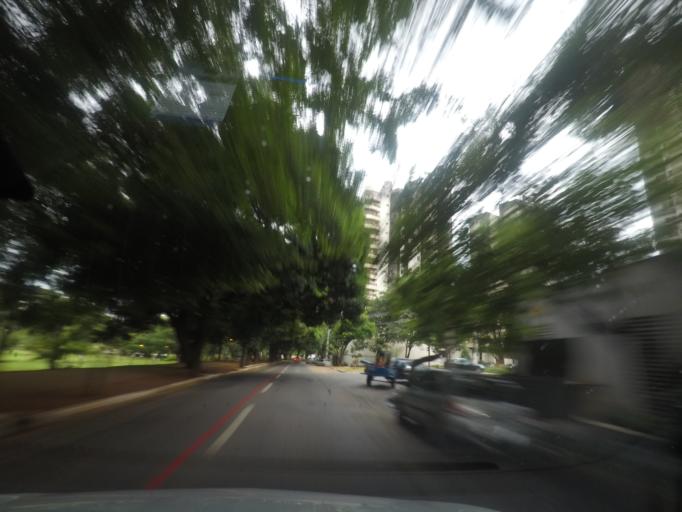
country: BR
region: Goias
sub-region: Goiania
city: Goiania
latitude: -16.6807
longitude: -49.2721
